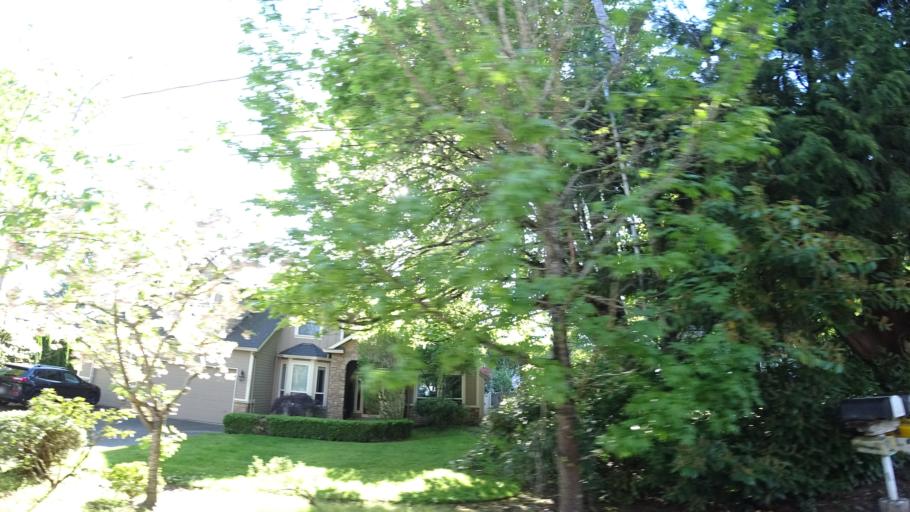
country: US
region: Oregon
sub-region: Washington County
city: West Slope
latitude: 45.4952
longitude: -122.7653
